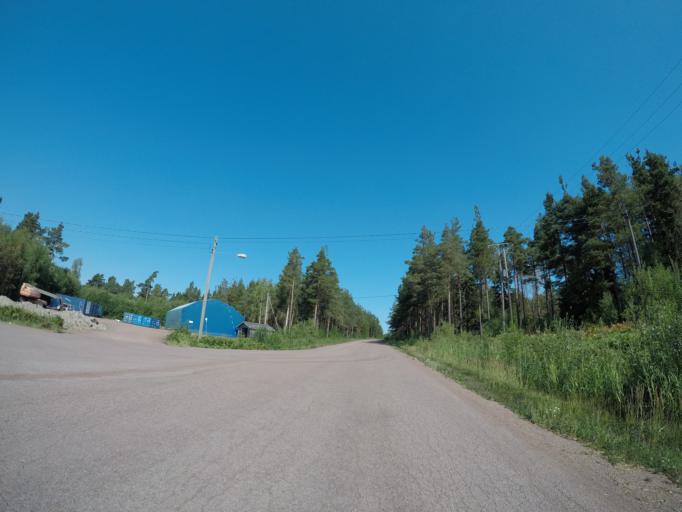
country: AX
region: Alands landsbygd
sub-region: Saltvik
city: Saltvik
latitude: 60.2286
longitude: 20.0086
